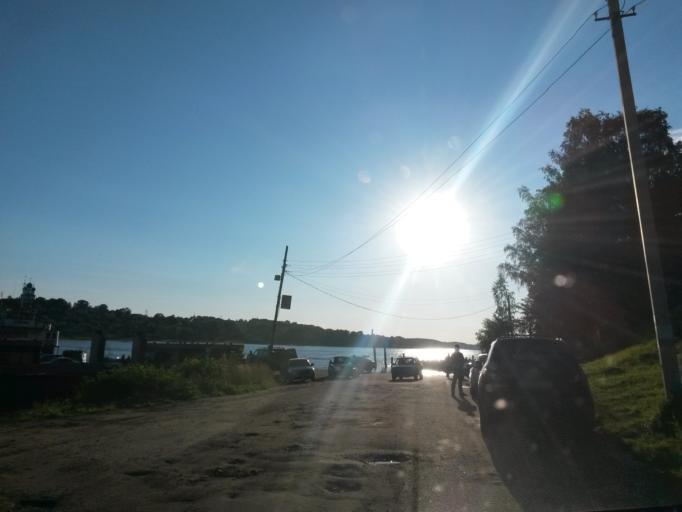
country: RU
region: Jaroslavl
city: Tutayev
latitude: 57.8779
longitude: 39.5415
